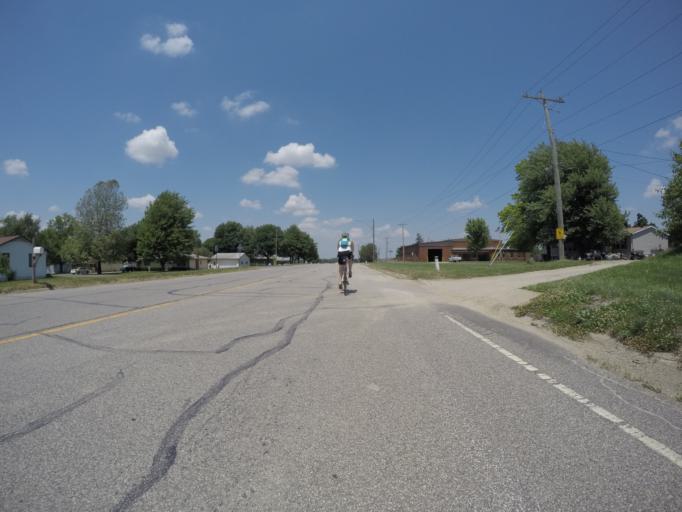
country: US
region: Kansas
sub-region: Doniphan County
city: Troy
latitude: 39.7802
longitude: -95.0970
